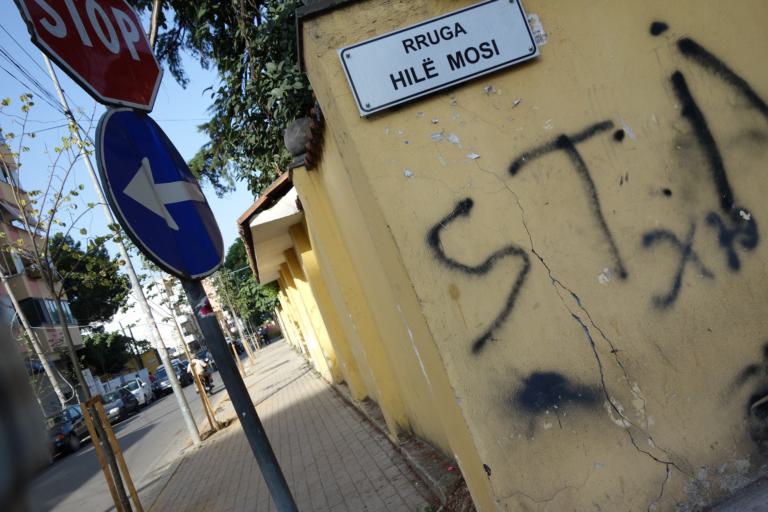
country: AL
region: Tirane
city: Tirana
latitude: 41.3333
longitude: 19.8299
